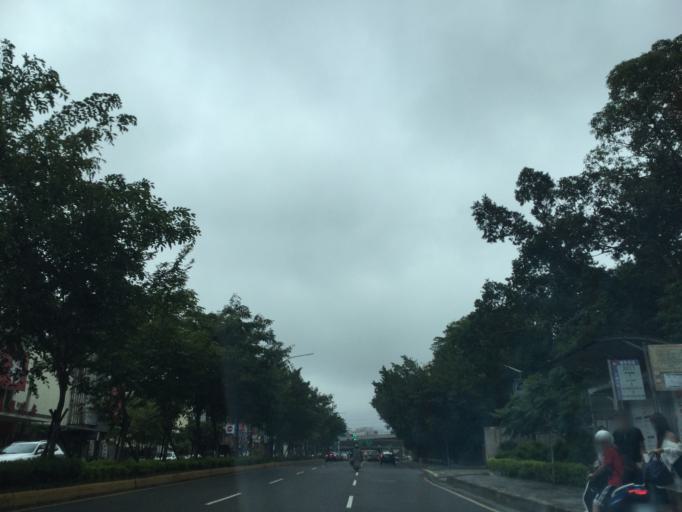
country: TW
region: Taiwan
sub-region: Hsinchu
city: Hsinchu
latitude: 24.7920
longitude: 121.0031
